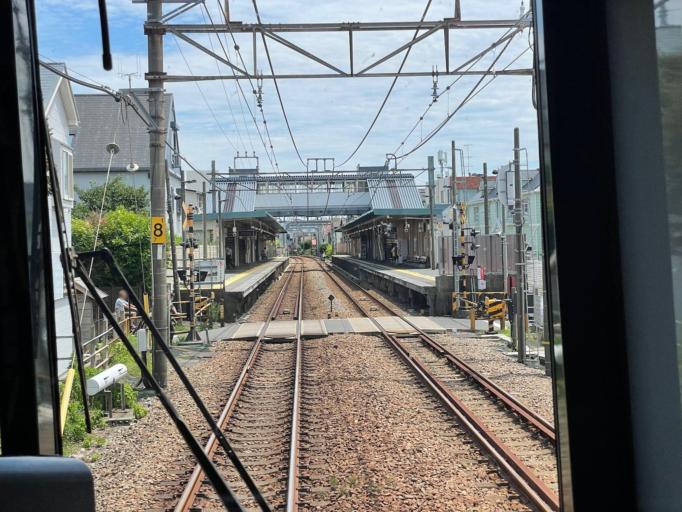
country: JP
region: Kanagawa
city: Fujisawa
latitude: 35.3213
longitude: 139.4713
